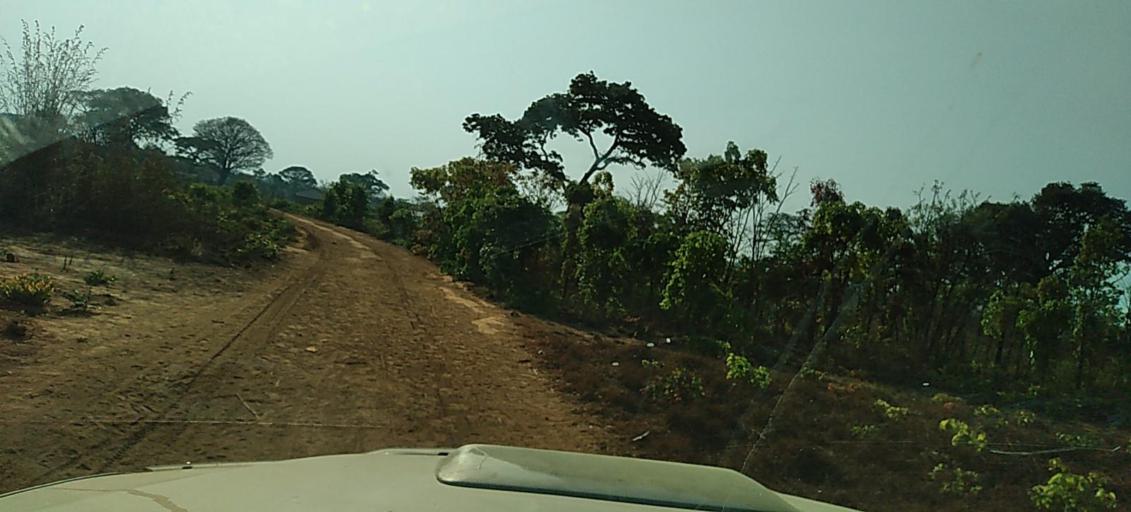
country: ZM
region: North-Western
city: Kasempa
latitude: -13.1857
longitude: 25.9641
